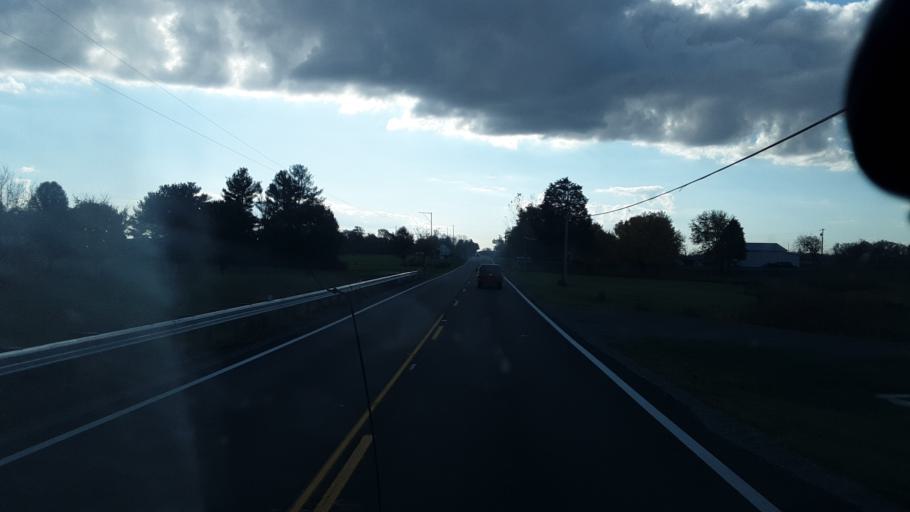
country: US
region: Ohio
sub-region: Fayette County
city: Washington Court House
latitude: 39.5690
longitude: -83.4657
